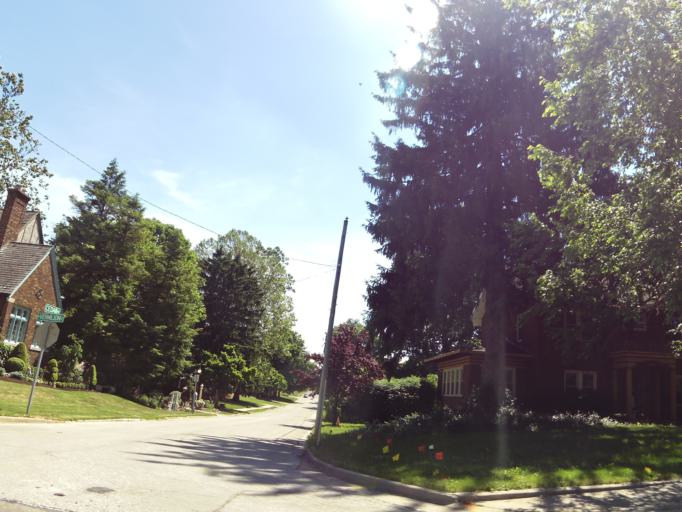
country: US
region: Illinois
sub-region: Vermilion County
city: Danville
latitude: 40.1646
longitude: -87.6305
